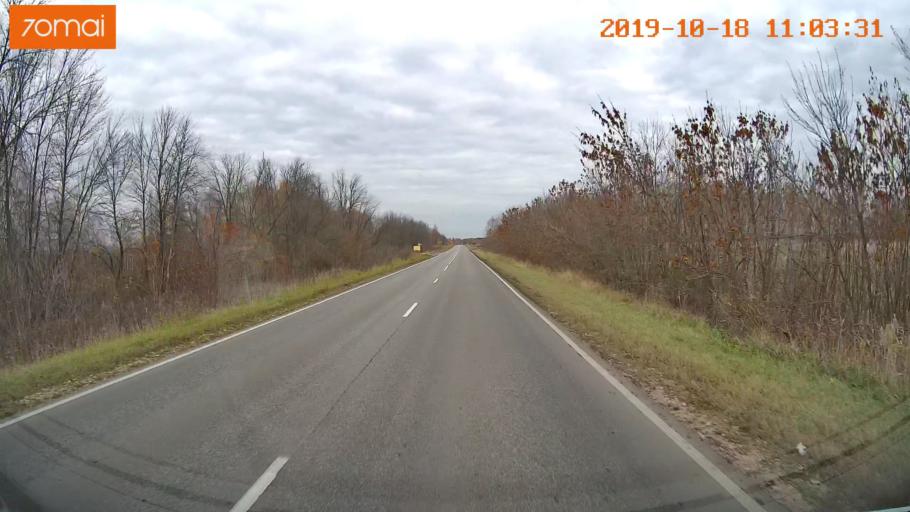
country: RU
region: Tula
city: Yepifan'
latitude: 53.8810
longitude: 38.5488
